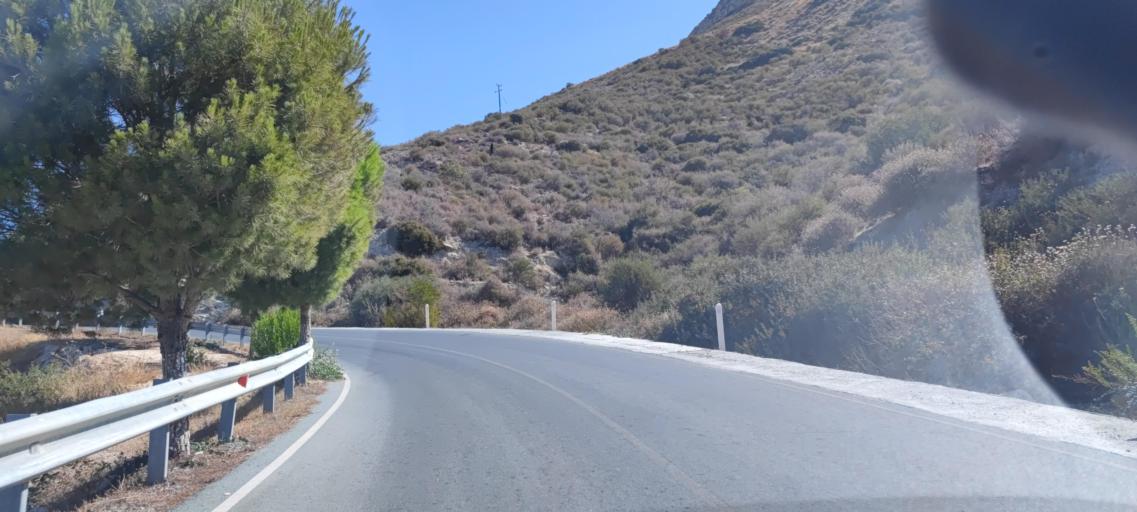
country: CY
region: Limassol
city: Mouttagiaka
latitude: 34.7439
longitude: 33.0879
